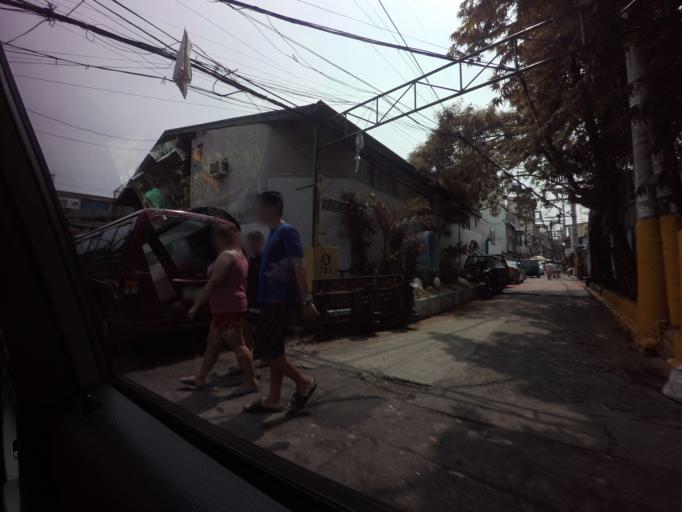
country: PH
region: Metro Manila
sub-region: City of Manila
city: Quiapo
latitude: 14.5711
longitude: 120.9961
